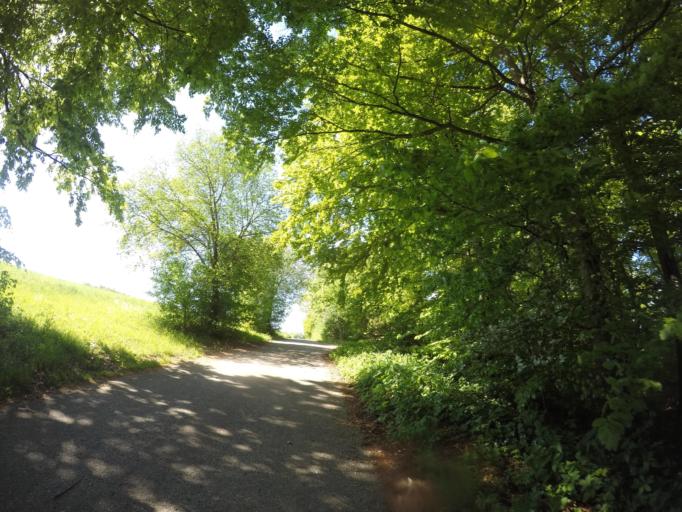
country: DE
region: Baden-Wuerttemberg
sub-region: Tuebingen Region
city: Laichingen
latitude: 48.4357
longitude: 9.6848
